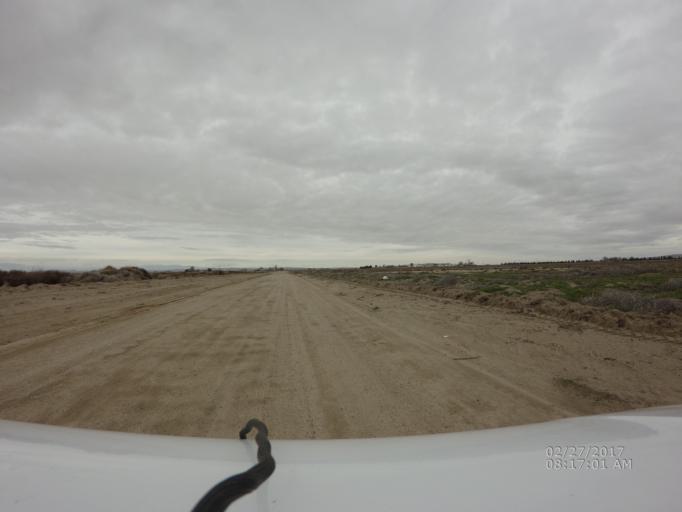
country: US
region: California
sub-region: Los Angeles County
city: Lancaster
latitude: 34.7073
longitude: -118.0145
